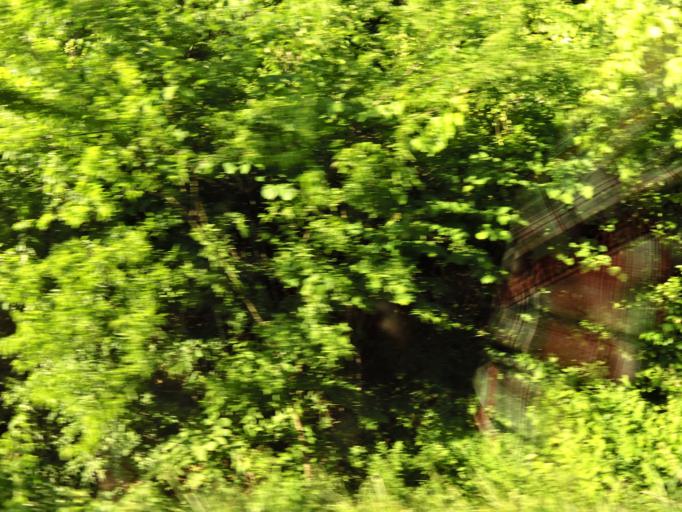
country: US
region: Tennessee
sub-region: Sevier County
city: Seymour
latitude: 35.8540
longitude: -83.7175
